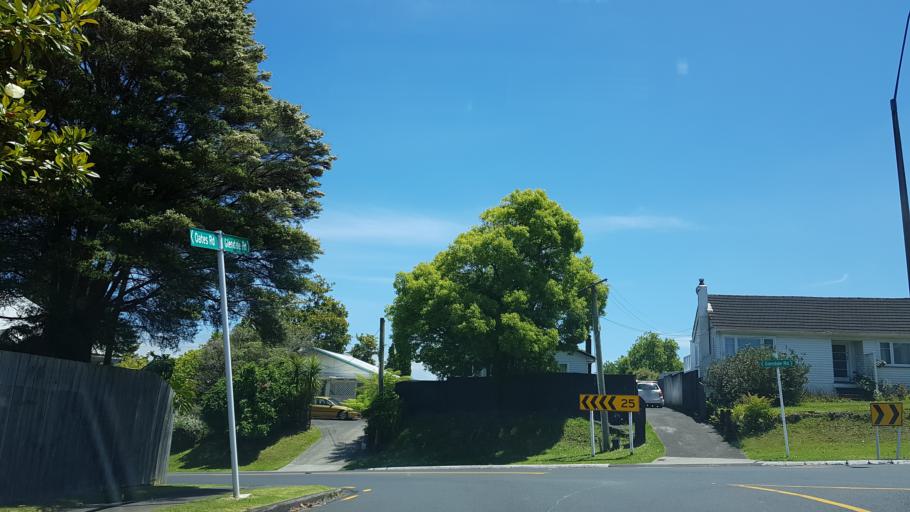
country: NZ
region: Auckland
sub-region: Auckland
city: Waitakere
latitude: -36.9112
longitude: 174.6497
